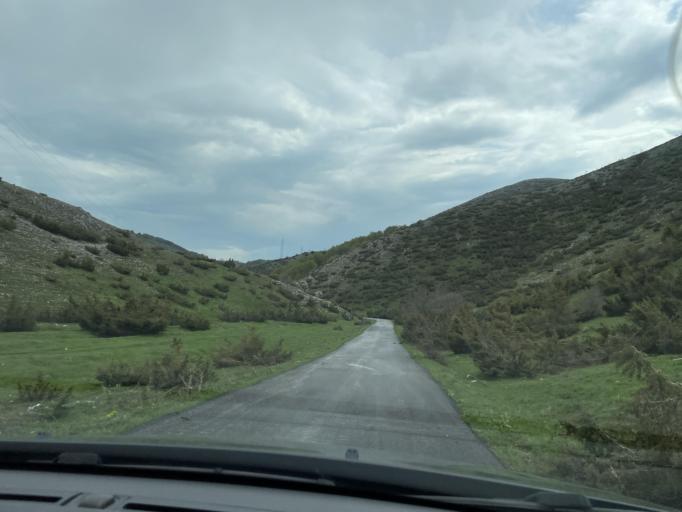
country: MK
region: Opstina Rostusa
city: Rostusha
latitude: 41.6122
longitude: 20.6804
